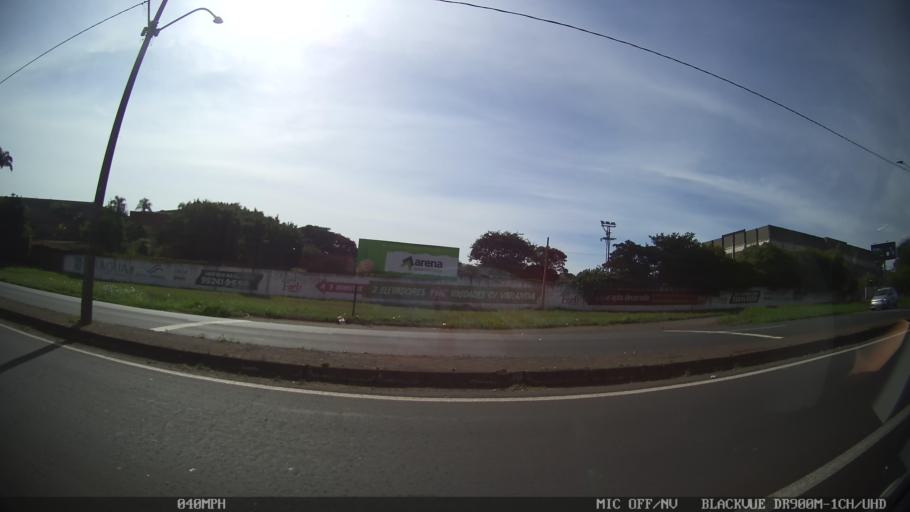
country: BR
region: Sao Paulo
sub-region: Piracicaba
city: Piracicaba
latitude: -22.6926
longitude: -47.6649
